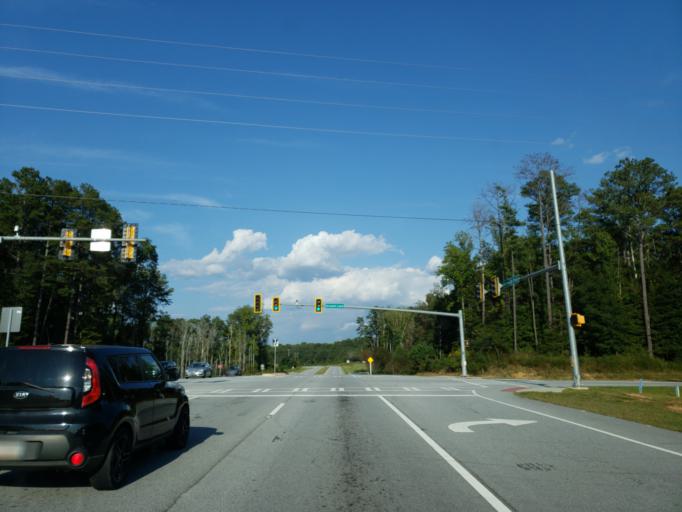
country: US
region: Georgia
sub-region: Paulding County
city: Hiram
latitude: 33.8611
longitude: -84.7485
